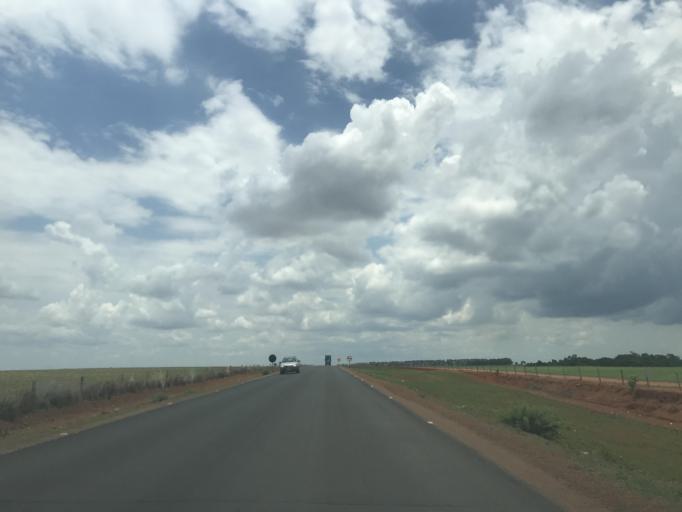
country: BR
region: Goias
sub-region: Vianopolis
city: Vianopolis
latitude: -16.7757
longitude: -48.5226
